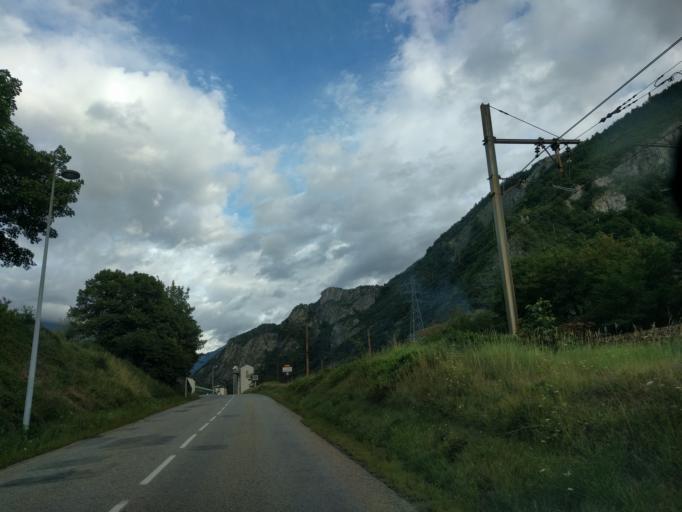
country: FR
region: Rhone-Alpes
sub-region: Departement de la Savoie
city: Villargondran
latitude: 45.2472
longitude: 6.4128
